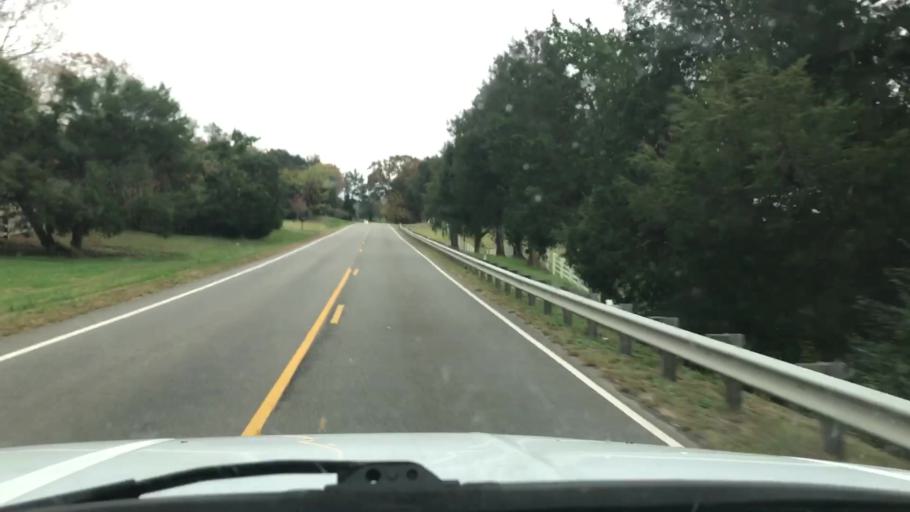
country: US
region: Virginia
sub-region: Goochland County
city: Goochland
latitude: 37.6423
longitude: -77.8160
